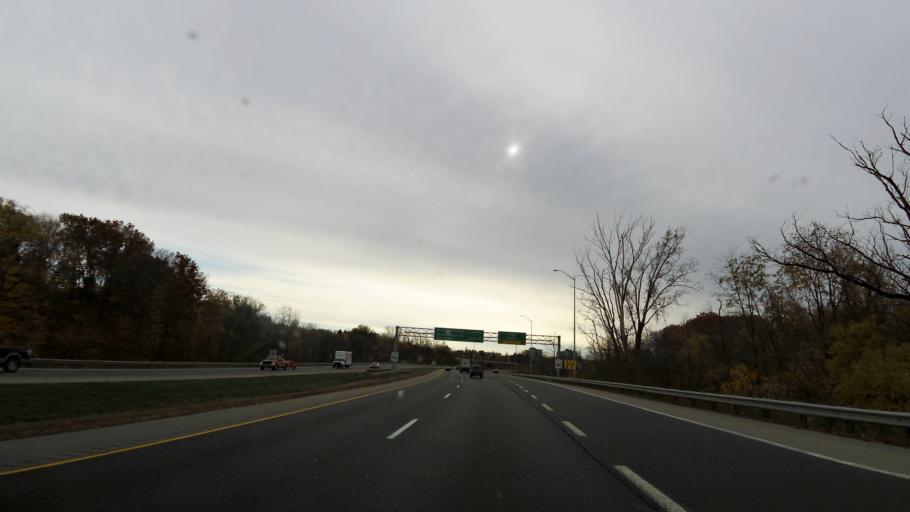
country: CA
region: Ontario
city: Hamilton
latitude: 43.2302
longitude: -79.7872
